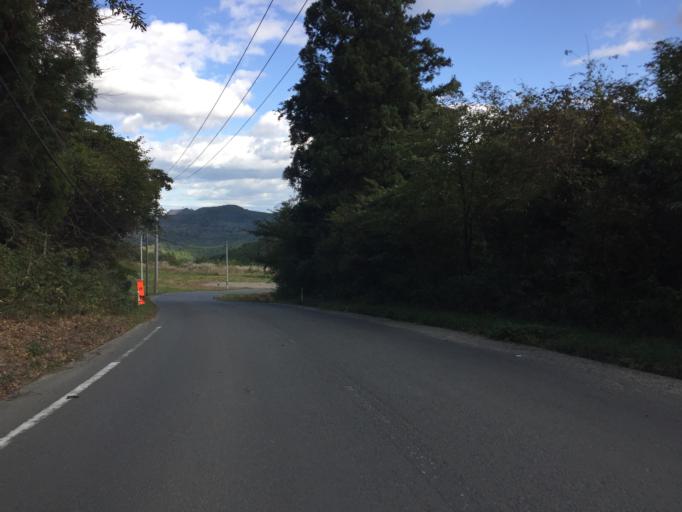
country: JP
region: Miyagi
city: Marumori
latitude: 37.8348
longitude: 140.8223
